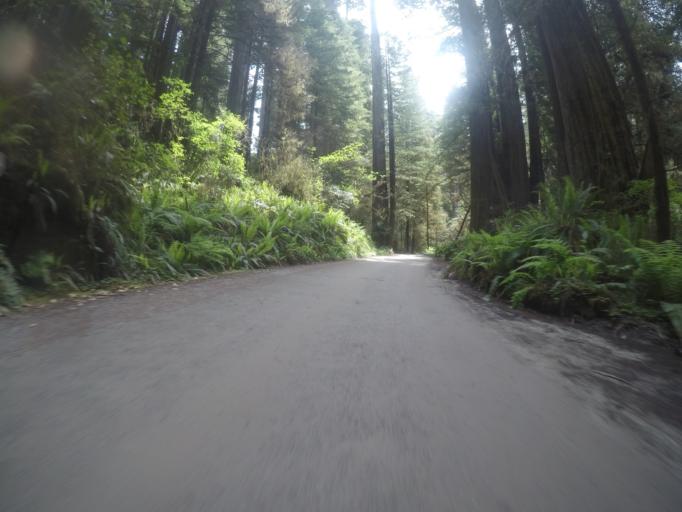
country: US
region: California
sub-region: Del Norte County
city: Bertsch-Oceanview
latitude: 41.7663
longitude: -124.1142
